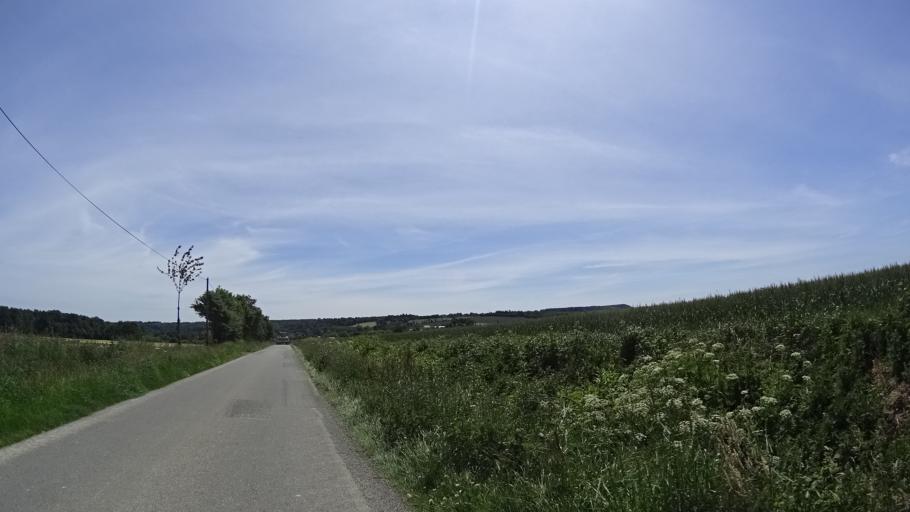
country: FR
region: Brittany
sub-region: Departement d'Ille-et-Vilaine
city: Iffendic
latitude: 48.1422
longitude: -1.9958
